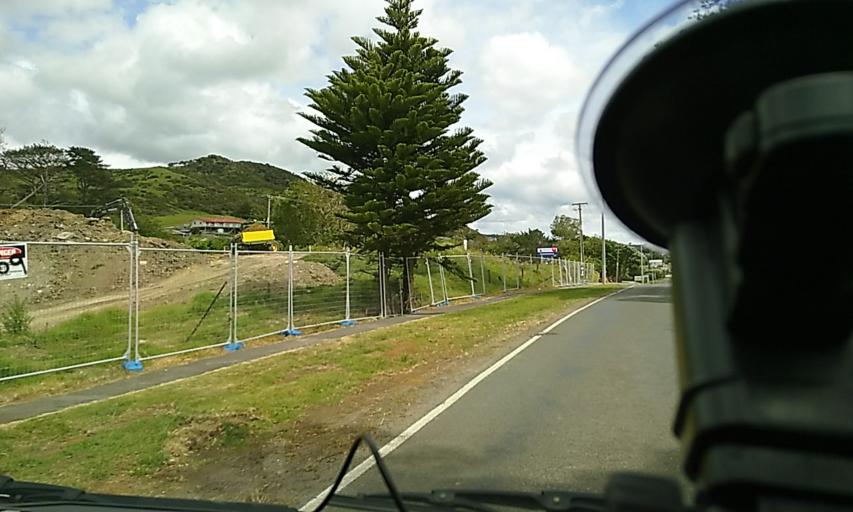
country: NZ
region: Northland
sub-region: Far North District
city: Ahipara
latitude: -35.5070
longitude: 173.3903
